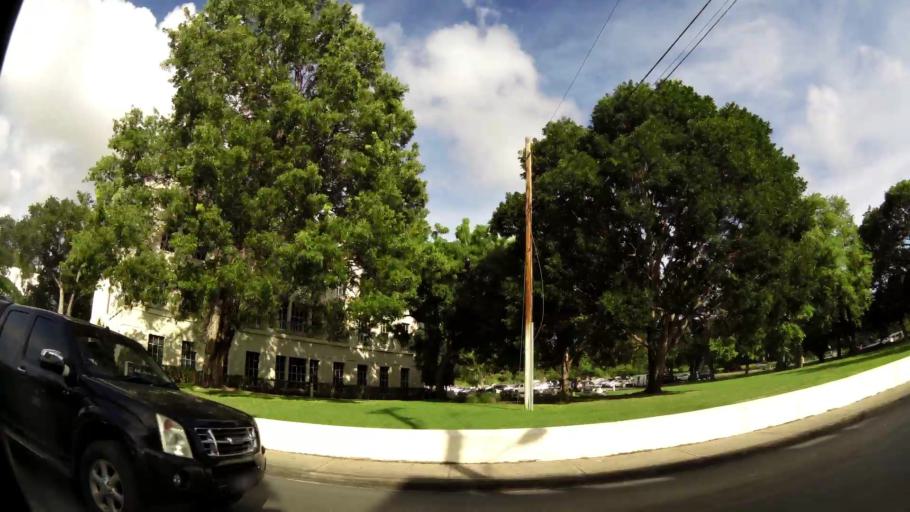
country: BB
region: Saint Michael
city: Bridgetown
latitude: 13.0923
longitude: -59.6016
